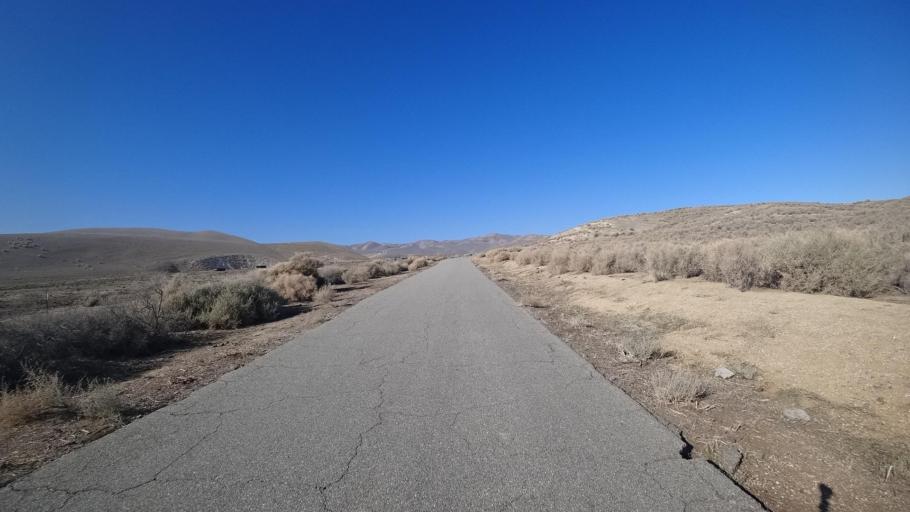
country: US
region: California
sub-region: Kern County
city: Taft Heights
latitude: 35.2319
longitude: -119.6520
